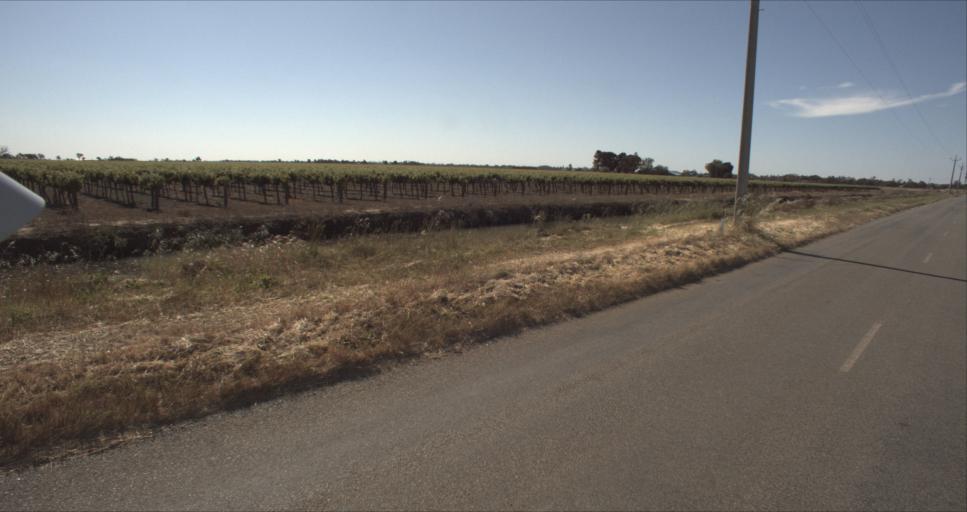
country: AU
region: New South Wales
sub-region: Leeton
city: Leeton
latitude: -34.5805
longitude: 146.3799
